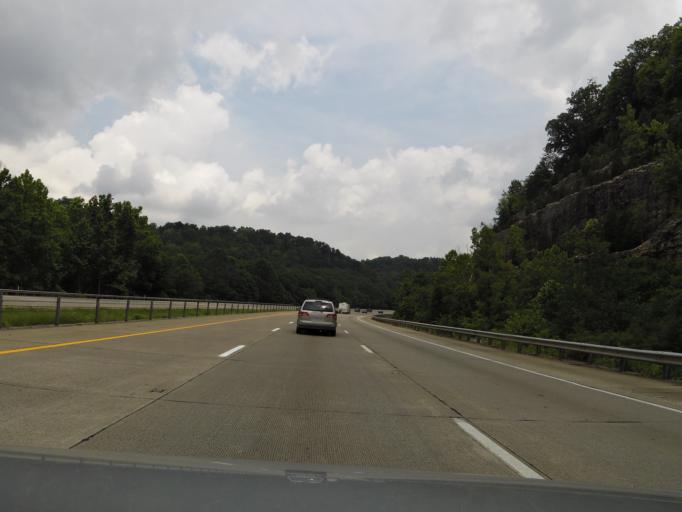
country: US
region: Kentucky
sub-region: Bullitt County
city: Lebanon Junction
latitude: 37.7659
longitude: -85.7924
